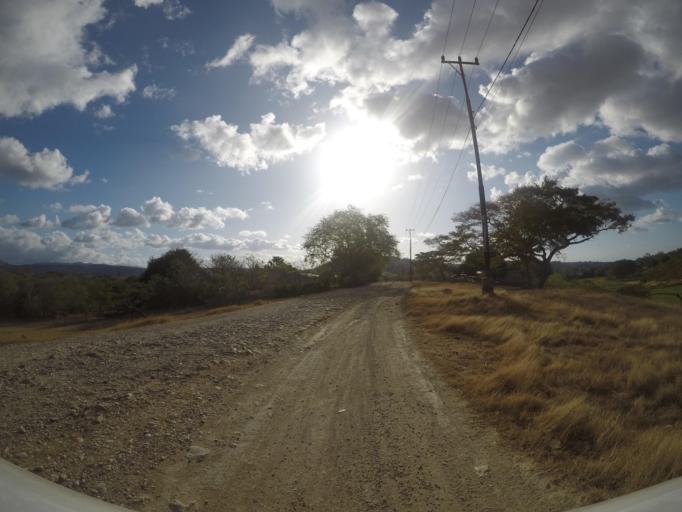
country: TL
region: Lautem
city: Lospalos
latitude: -8.4277
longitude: 126.8373
